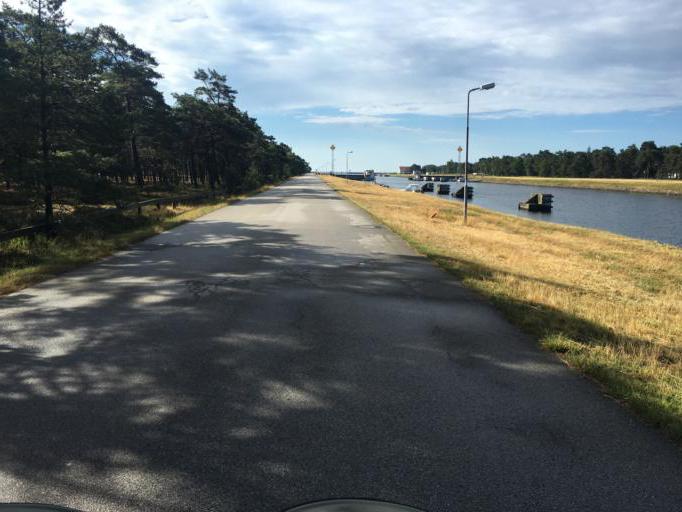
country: SE
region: Skane
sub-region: Vellinge Kommun
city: Hollviken
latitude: 55.4046
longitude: 12.9403
